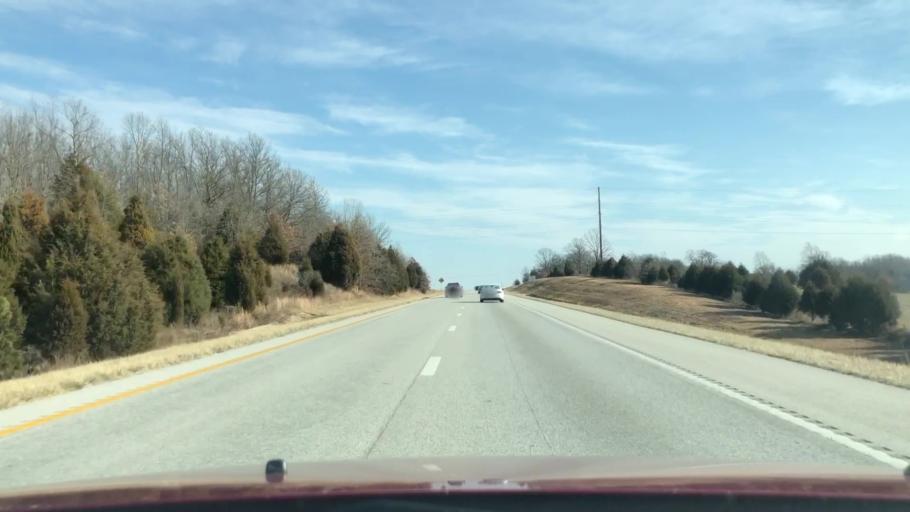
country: US
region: Missouri
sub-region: Webster County
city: Rogersville
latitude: 37.1205
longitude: -93.0064
